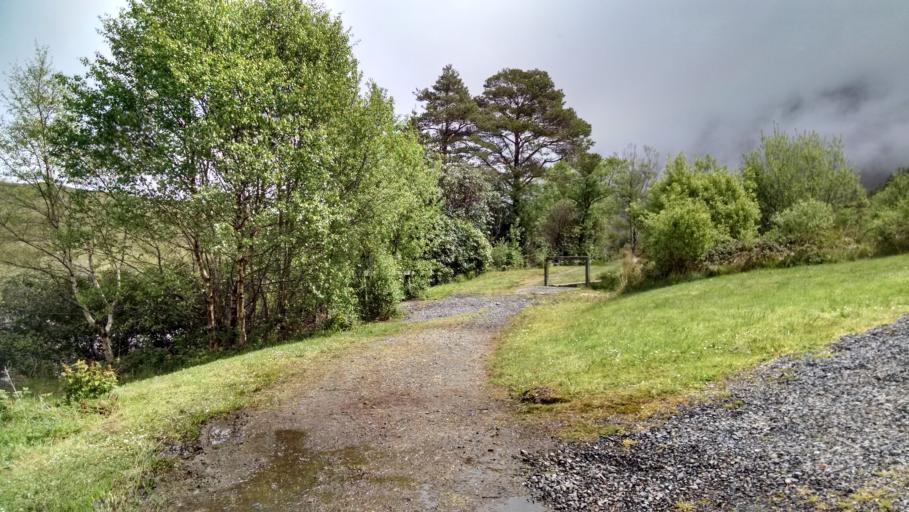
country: IE
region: Connaught
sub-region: Maigh Eo
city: Westport
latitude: 53.6197
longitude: -9.6691
